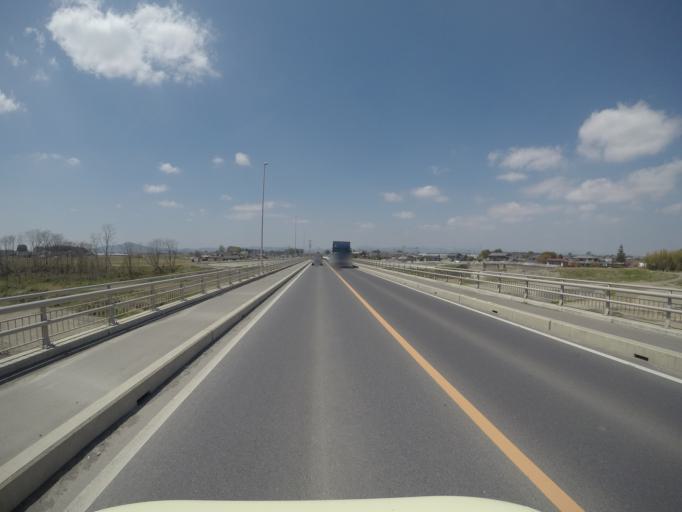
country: JP
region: Tochigi
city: Mibu
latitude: 36.3902
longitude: 139.7947
